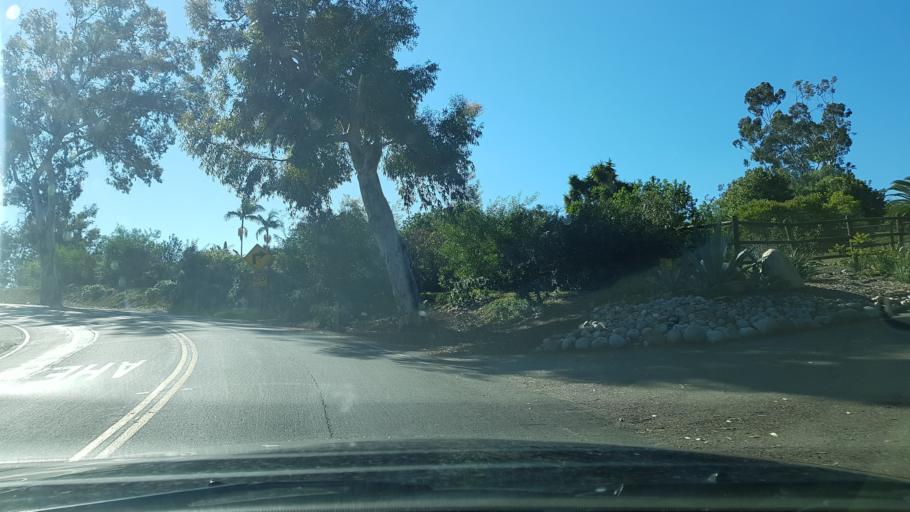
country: US
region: California
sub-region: San Diego County
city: Rancho Santa Fe
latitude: 33.0389
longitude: -117.2116
